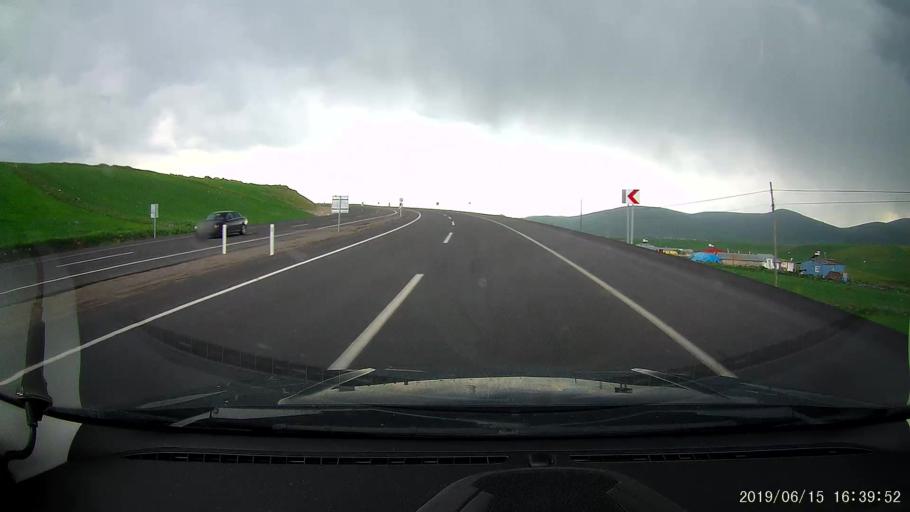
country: TR
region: Ardahan
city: Haskoy
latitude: 40.9775
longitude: 42.8936
